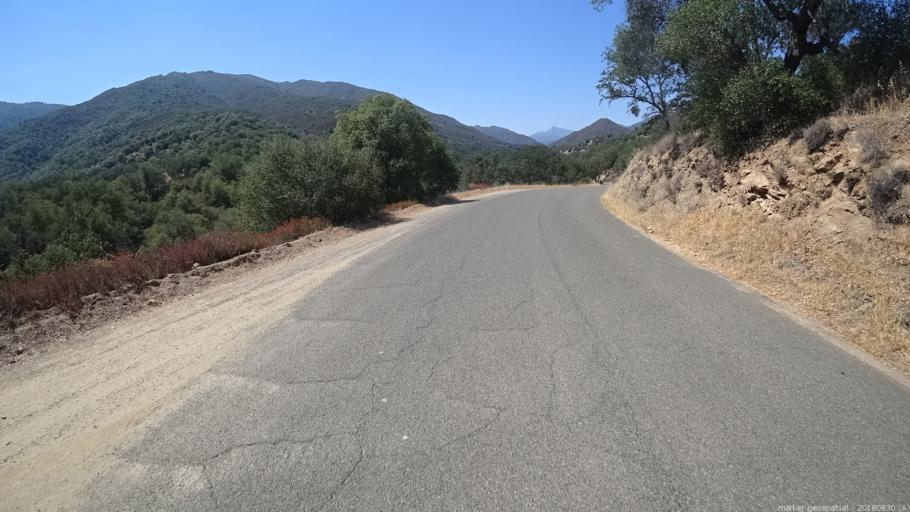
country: US
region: California
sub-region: Monterey County
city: King City
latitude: 35.9873
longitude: -121.3550
